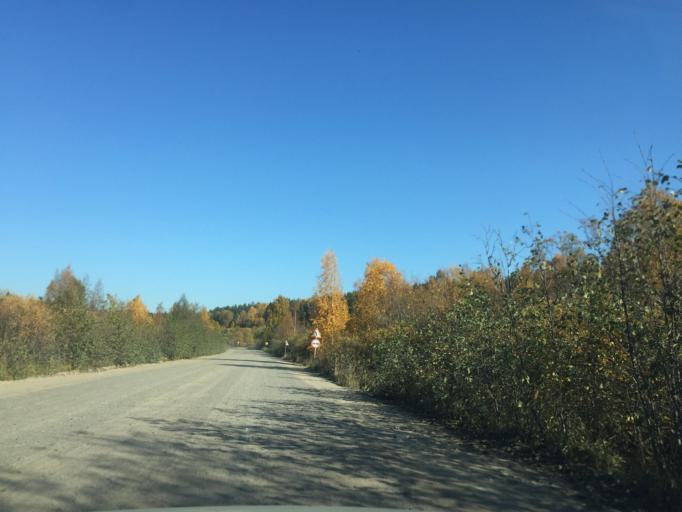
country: RU
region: Leningrad
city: Kuznechnoye
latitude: 61.3106
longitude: 29.9386
